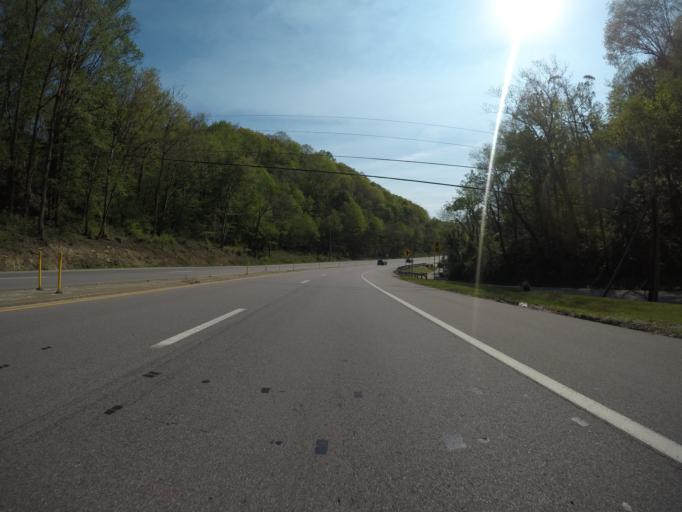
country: US
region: West Virginia
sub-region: Kanawha County
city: Charleston
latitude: 38.3441
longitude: -81.6081
